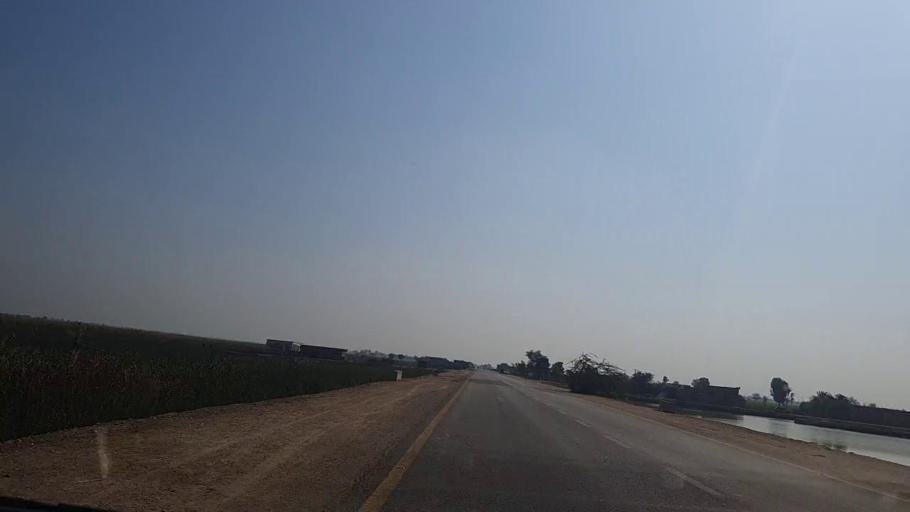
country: PK
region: Sindh
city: Sakrand
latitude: 26.0764
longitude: 68.4044
